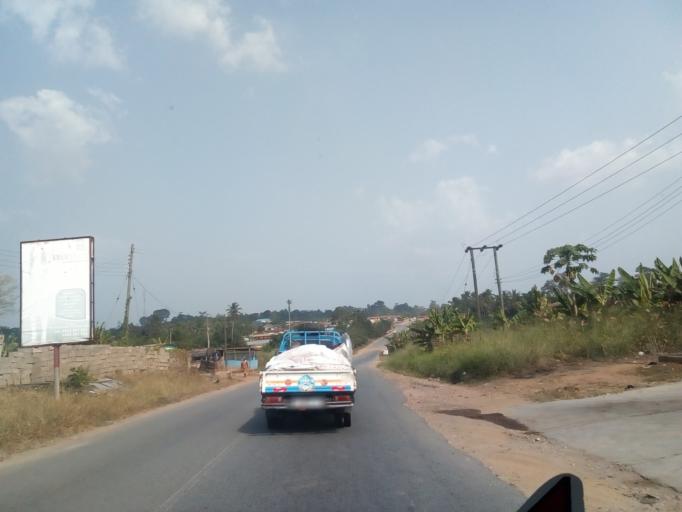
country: GH
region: Eastern
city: Suhum
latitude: 6.0449
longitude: -0.4173
